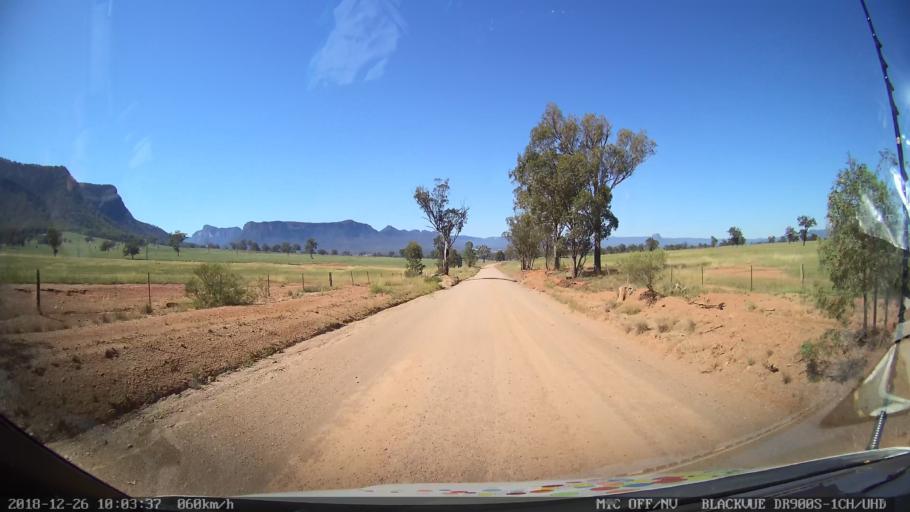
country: AU
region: New South Wales
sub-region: Mid-Western Regional
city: Kandos
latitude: -33.0631
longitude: 150.2174
